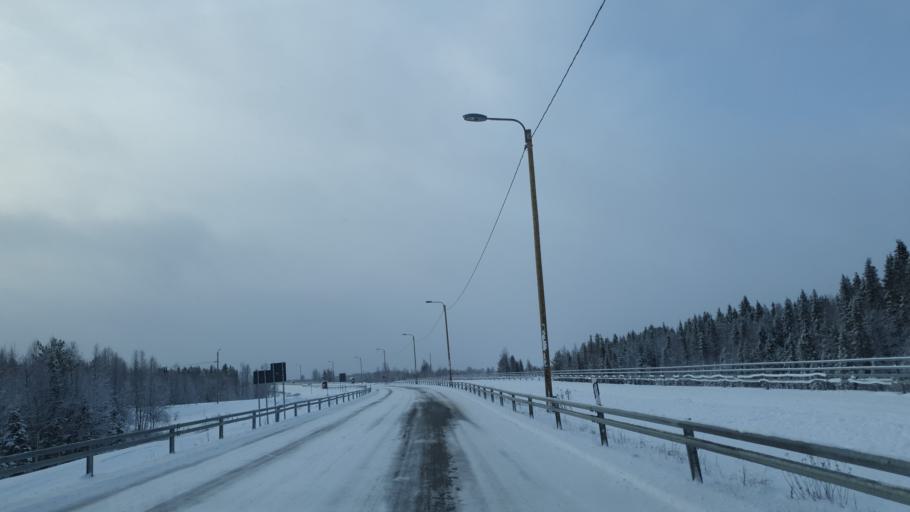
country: FI
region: Lapland
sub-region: Tunturi-Lappi
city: Kittilae
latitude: 67.4892
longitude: 24.9041
